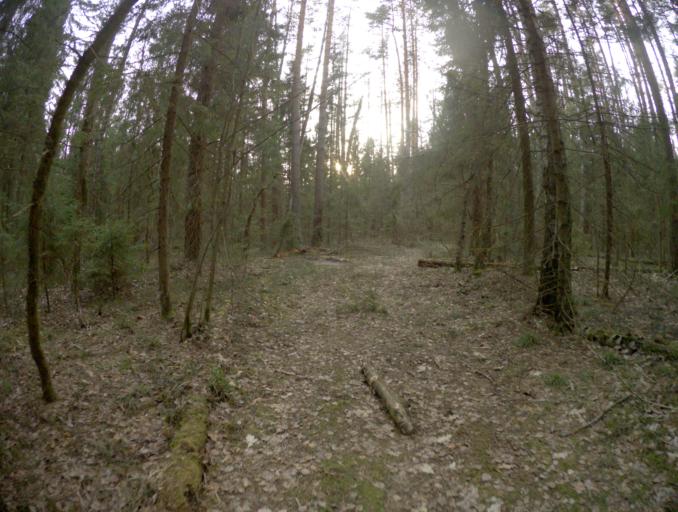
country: RU
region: Vladimir
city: Kommunar
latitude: 56.0829
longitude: 40.5166
